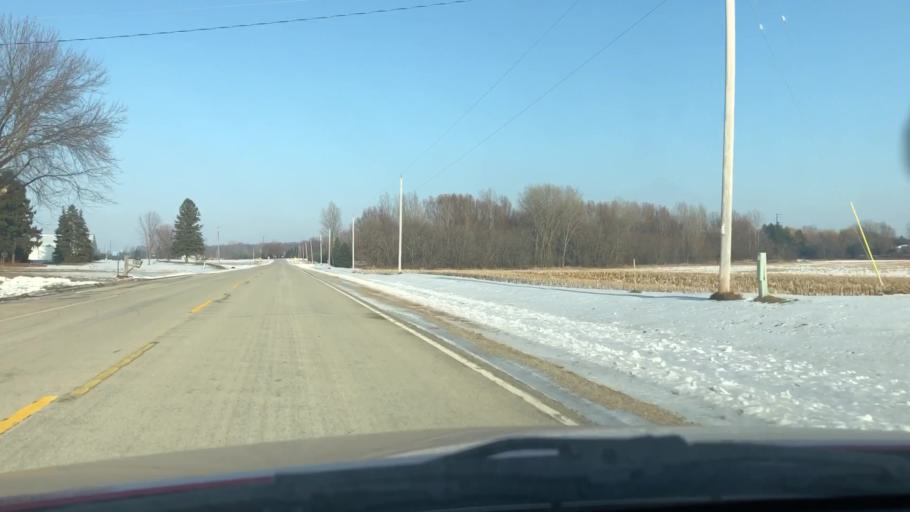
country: US
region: Wisconsin
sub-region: Outagamie County
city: Seymour
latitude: 44.4243
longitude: -88.3663
